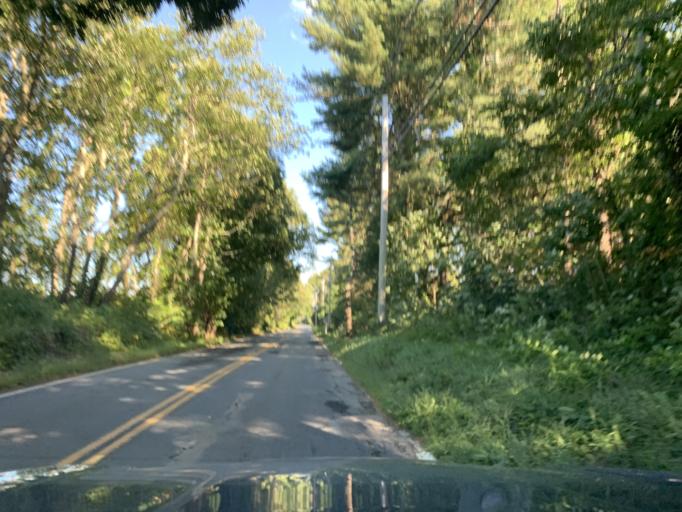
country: US
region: Rhode Island
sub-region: Washington County
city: Exeter
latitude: 41.5445
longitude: -71.5194
